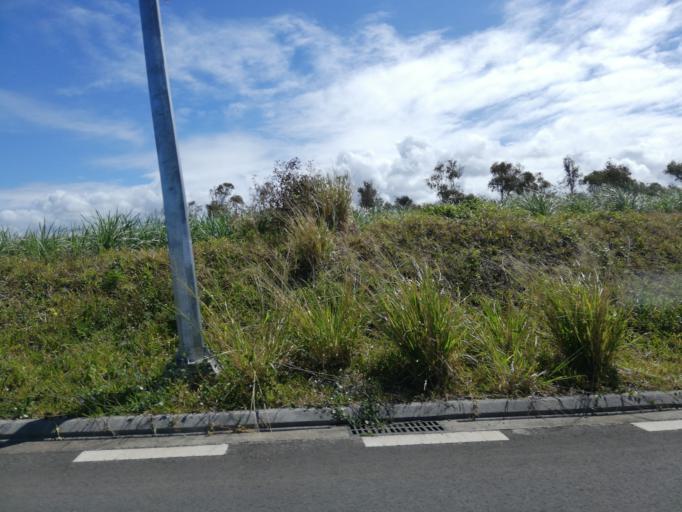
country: MU
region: Grand Port
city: Beau Vallon
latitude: -20.4482
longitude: 57.6970
